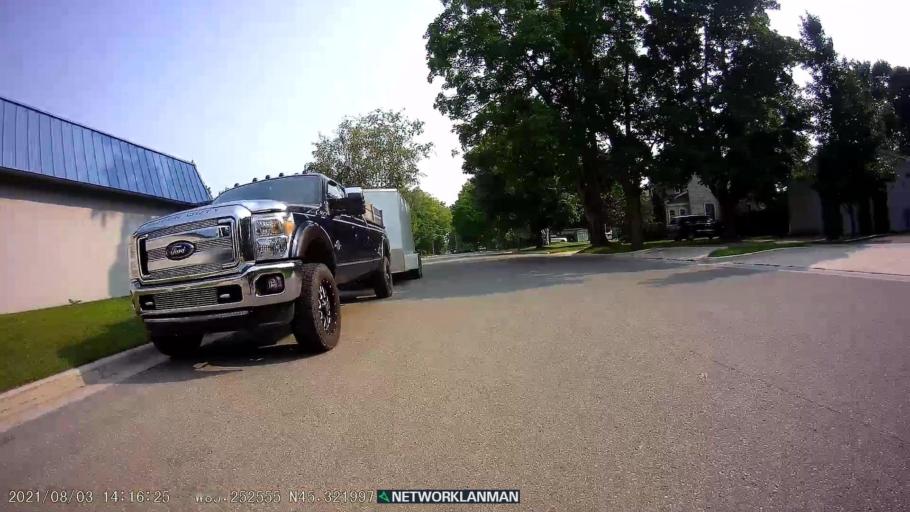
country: US
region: Michigan
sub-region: Charlevoix County
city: Charlevoix
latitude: 45.3222
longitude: -85.2526
